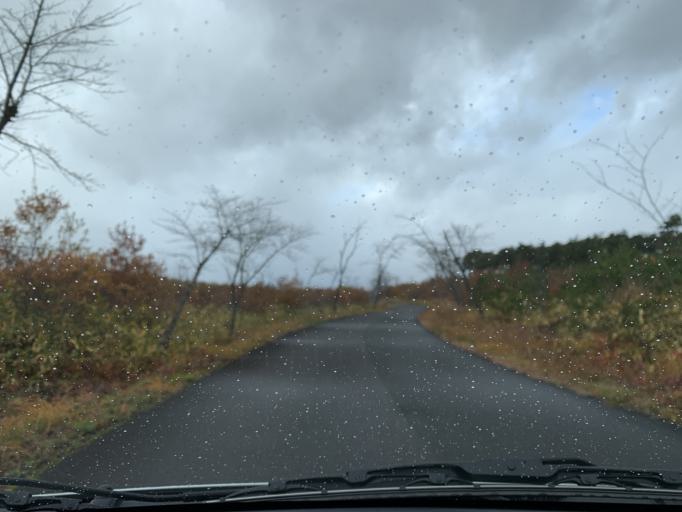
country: JP
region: Iwate
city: Mizusawa
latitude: 39.0844
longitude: 141.0158
